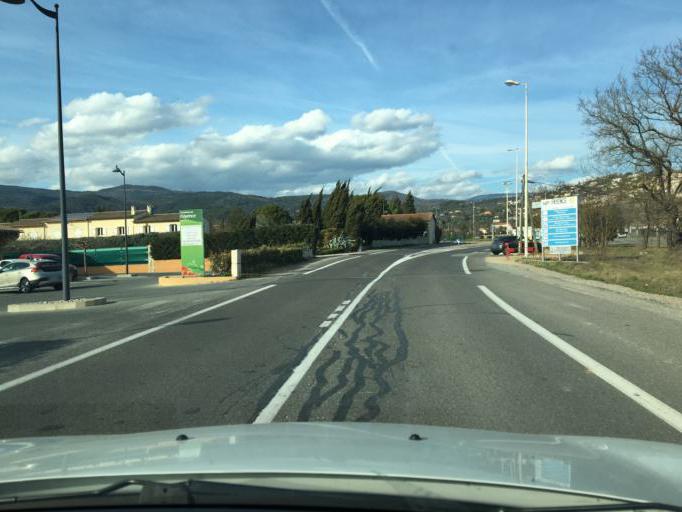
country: FR
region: Provence-Alpes-Cote d'Azur
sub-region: Departement du Var
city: Fayence
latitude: 43.6134
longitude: 6.6872
